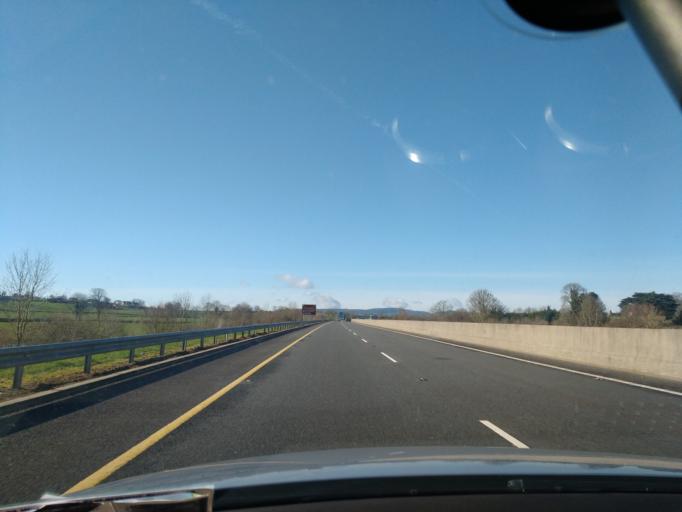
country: IE
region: Munster
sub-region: North Tipperary
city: Nenagh
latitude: 52.8446
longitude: -8.2122
